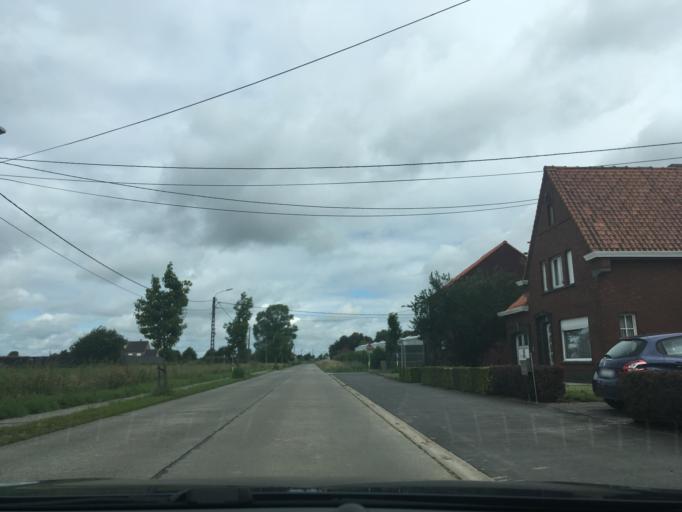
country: BE
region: Flanders
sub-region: Provincie West-Vlaanderen
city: Hooglede
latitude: 50.9537
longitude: 3.0592
